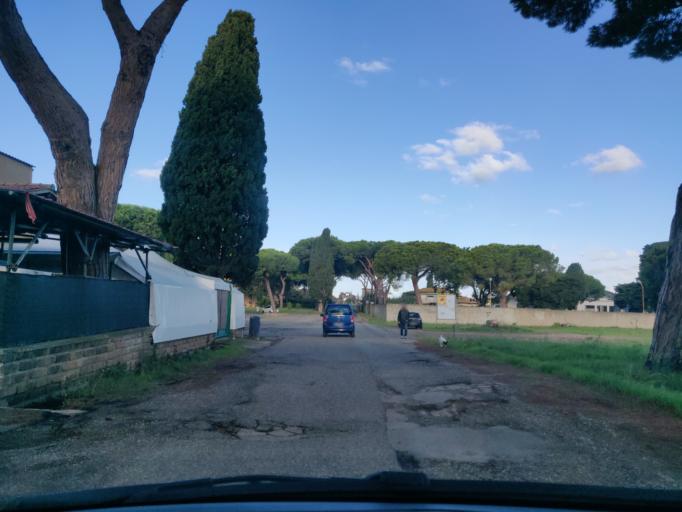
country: IT
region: Latium
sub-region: Citta metropolitana di Roma Capitale
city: Aurelia
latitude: 42.1381
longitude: 11.7857
